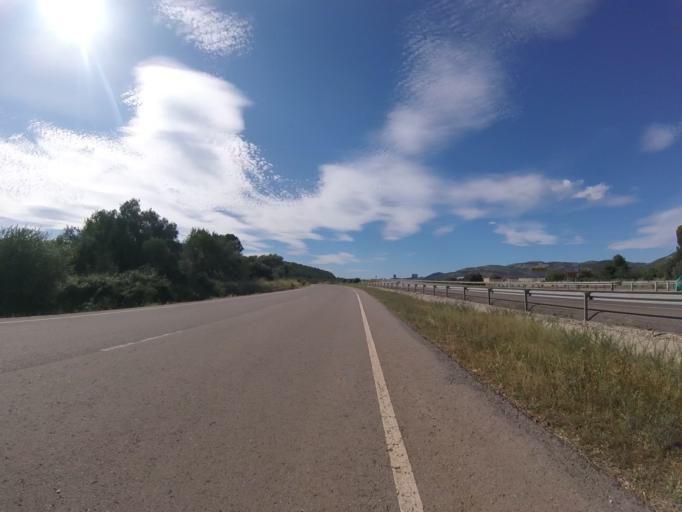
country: ES
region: Valencia
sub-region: Provincia de Castello
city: Peniscola
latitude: 40.3959
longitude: 0.3616
